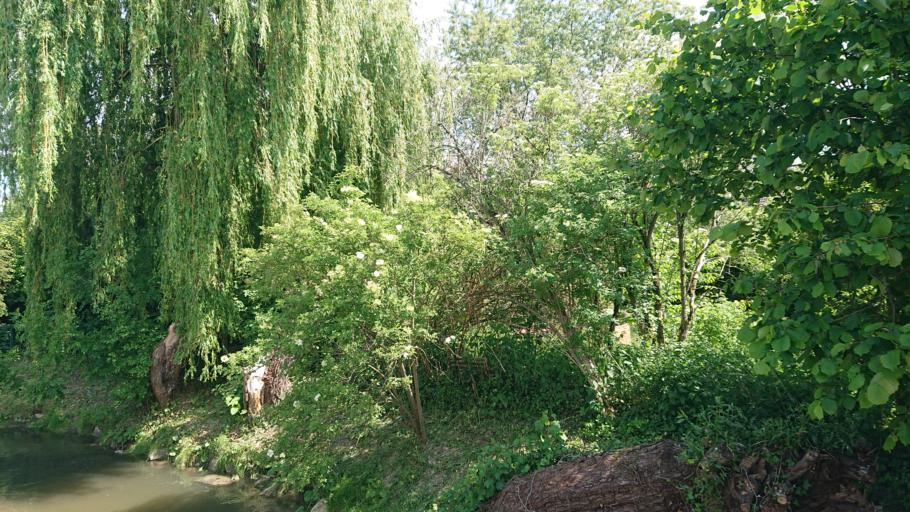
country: DE
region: North Rhine-Westphalia
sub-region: Regierungsbezirk Dusseldorf
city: Ratingen
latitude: 51.3353
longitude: 6.7840
